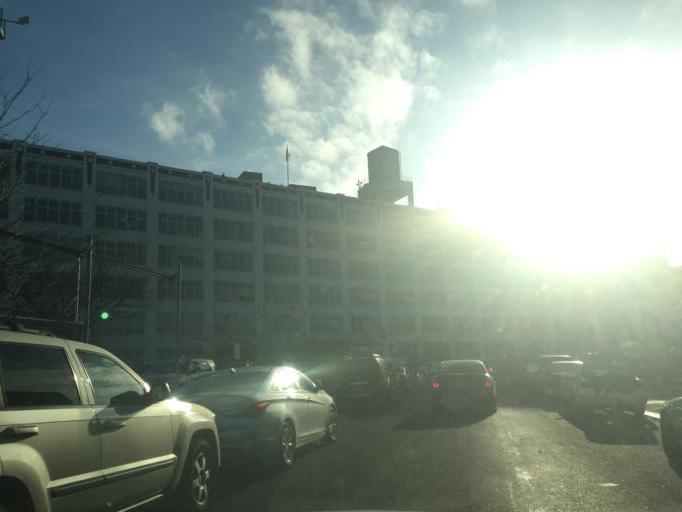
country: US
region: New York
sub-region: Queens County
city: Long Island City
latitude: 40.7527
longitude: -73.9253
